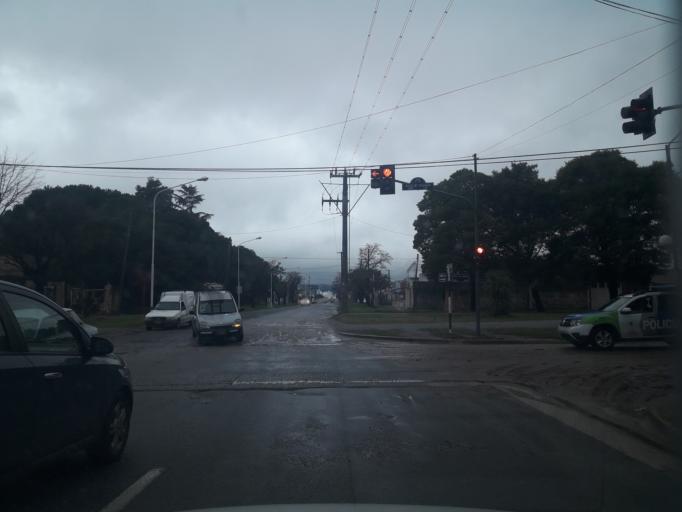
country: AR
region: Buenos Aires
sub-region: Partido de Tandil
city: Tandil
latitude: -37.3084
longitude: -59.1602
